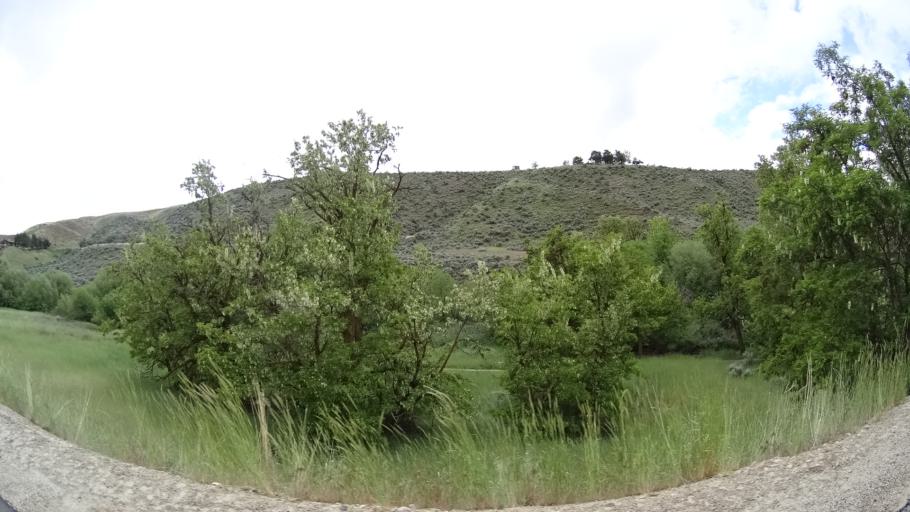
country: US
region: Idaho
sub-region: Ada County
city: Garden City
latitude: 43.6833
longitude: -116.2556
